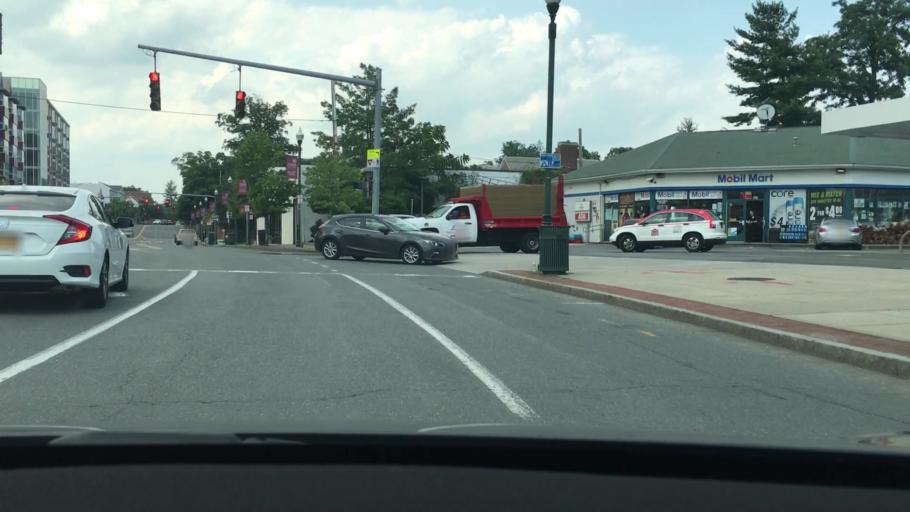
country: US
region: New York
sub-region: Westchester County
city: New Rochelle
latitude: 40.9238
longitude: -73.7877
